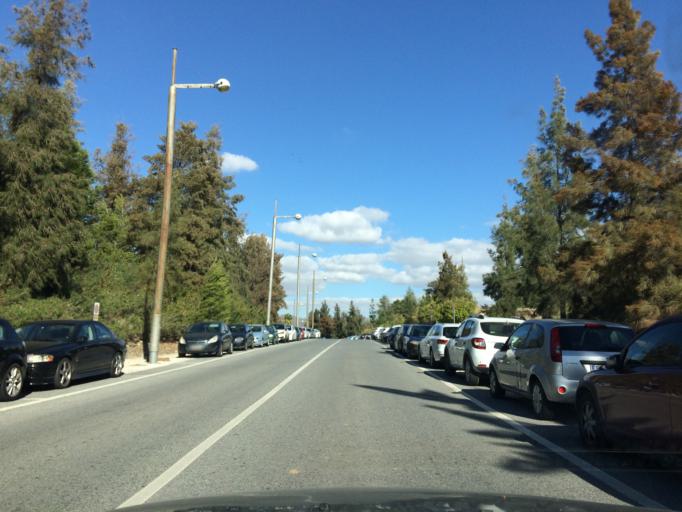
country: ES
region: Andalusia
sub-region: Provincia de Malaga
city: Estacion de Cartama
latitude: 36.7349
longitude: -4.5469
